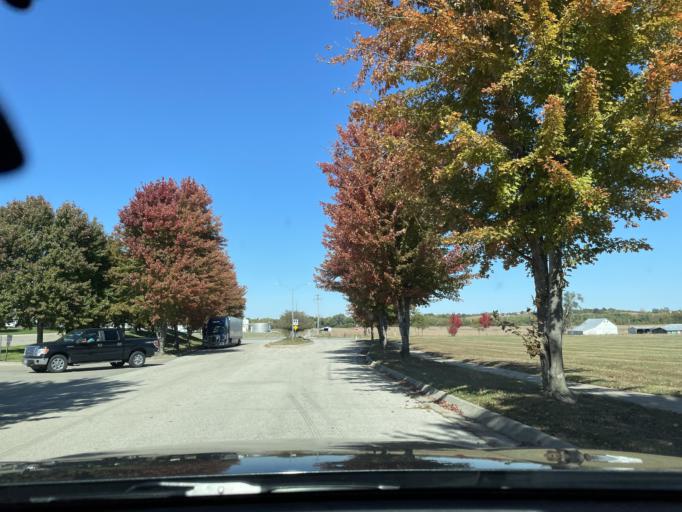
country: US
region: Missouri
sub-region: Buchanan County
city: Saint Joseph
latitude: 39.7542
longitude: -94.7567
